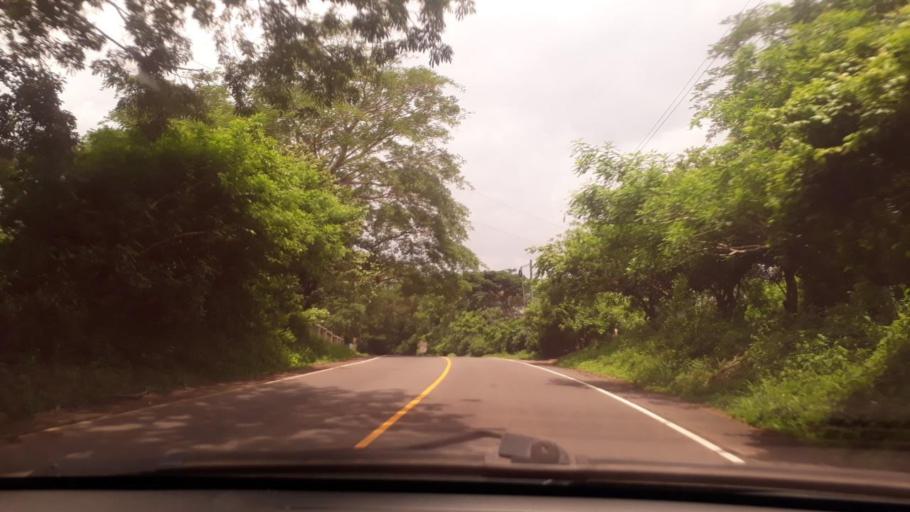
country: GT
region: Santa Rosa
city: Cuilapa
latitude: 14.2213
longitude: -90.3366
